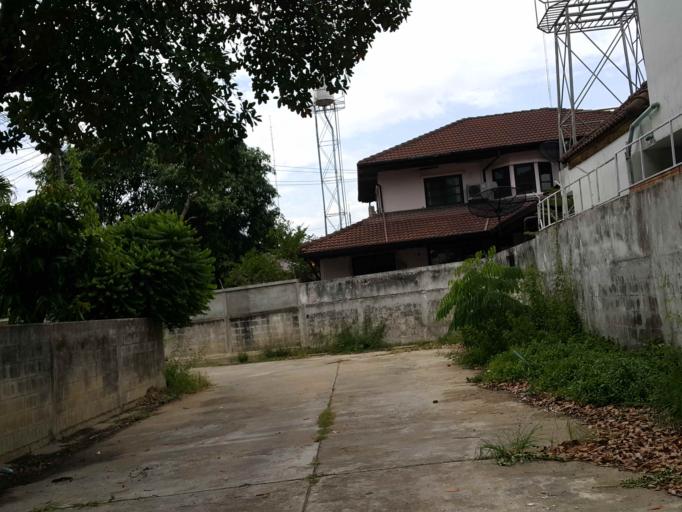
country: TH
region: Chiang Mai
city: Chiang Mai
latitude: 18.7637
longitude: 99.0230
